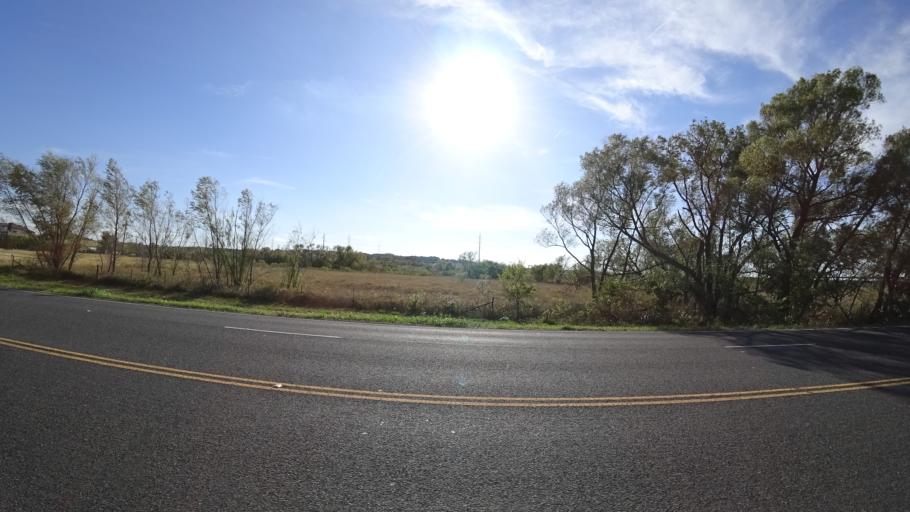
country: US
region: Texas
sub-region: Travis County
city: Wells Branch
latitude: 30.4730
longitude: -97.6914
